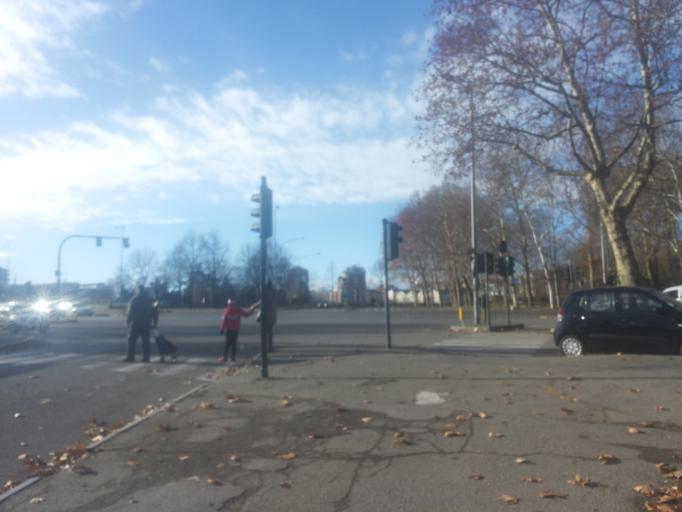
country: IT
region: Piedmont
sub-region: Provincia di Torino
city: Lesna
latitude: 45.0568
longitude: 7.6354
